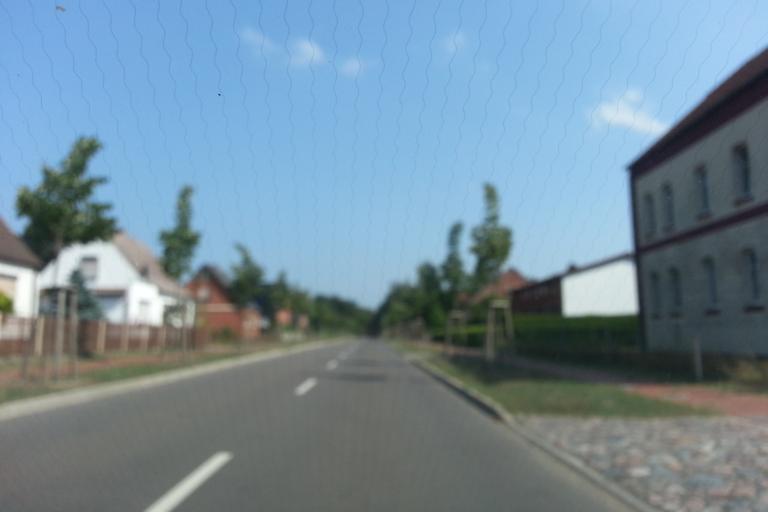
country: DE
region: Mecklenburg-Vorpommern
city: Strasburg
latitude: 53.6075
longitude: 13.7895
